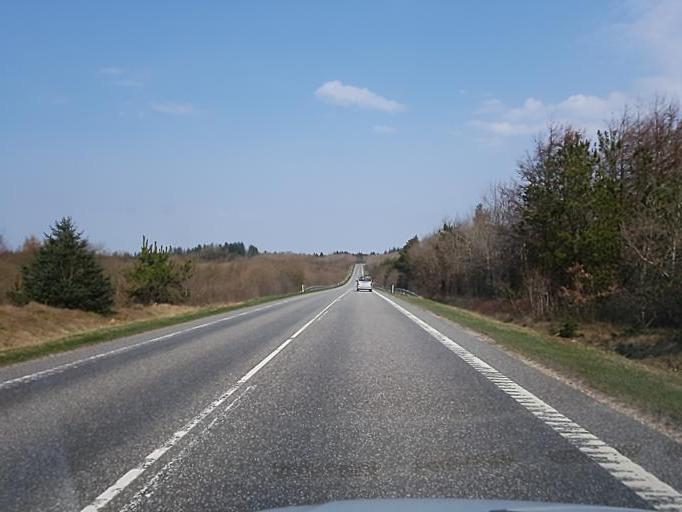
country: DK
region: Central Jutland
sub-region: Ringkobing-Skjern Kommune
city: Tarm
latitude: 55.8389
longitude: 8.4919
